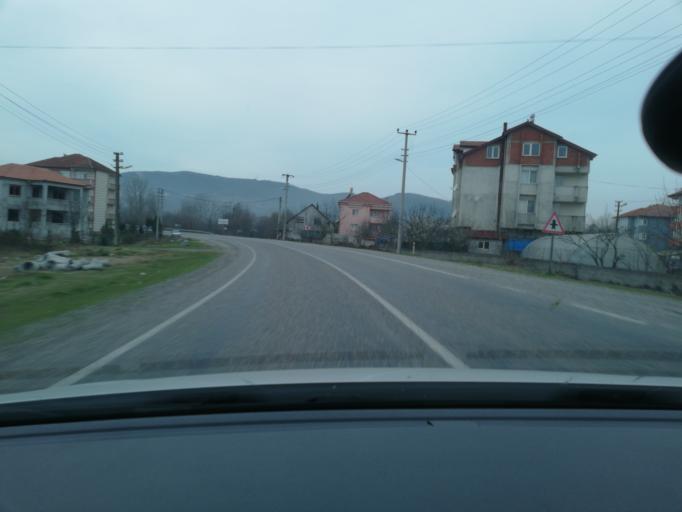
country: TR
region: Zonguldak
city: Saltukova
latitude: 41.5270
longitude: 32.0978
